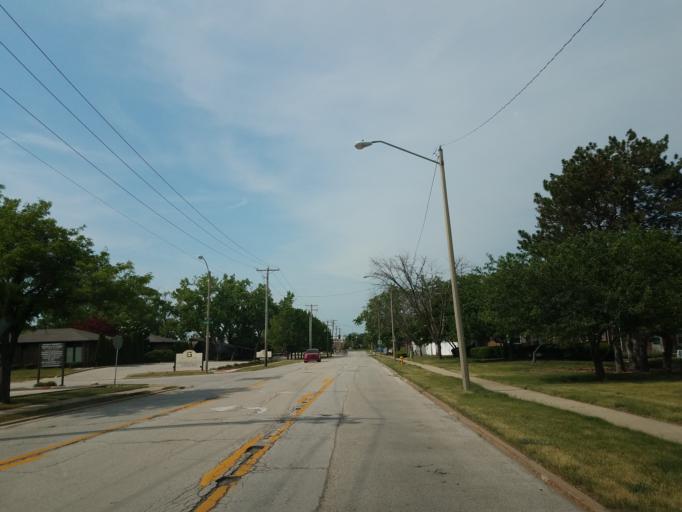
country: US
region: Illinois
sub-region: McLean County
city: Bloomington
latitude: 40.4783
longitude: -88.9503
